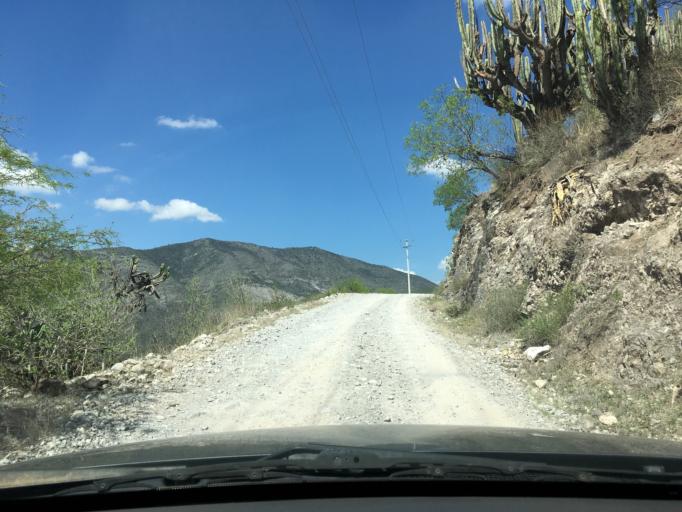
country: MX
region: Hidalgo
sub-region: Metztitlan
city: Fontezuelas
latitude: 20.6343
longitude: -98.8432
